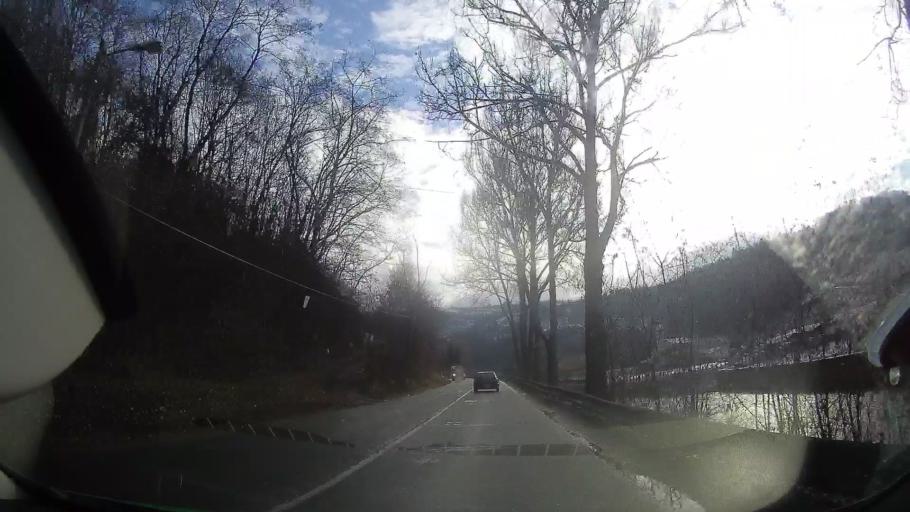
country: RO
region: Alba
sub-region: Oras Campeni
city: Campeni
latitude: 46.3617
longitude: 23.0611
